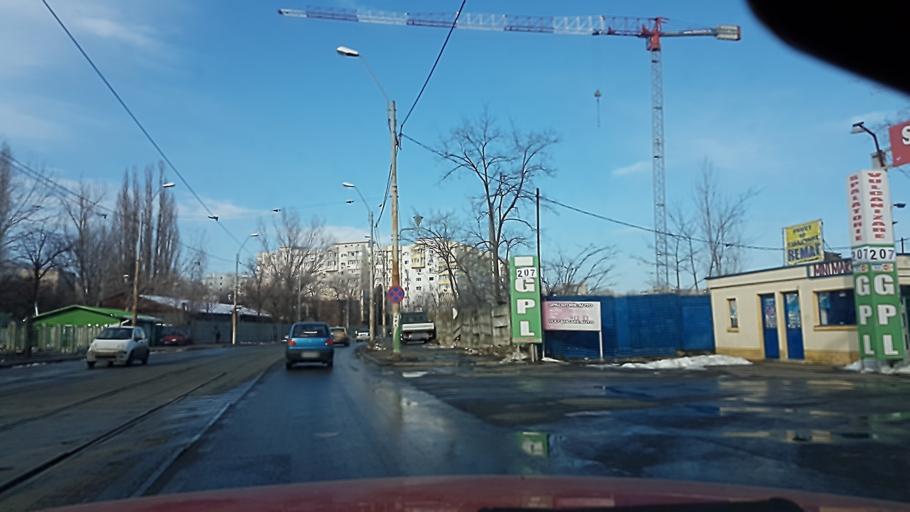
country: RO
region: Ilfov
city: Dobroesti
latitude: 44.4317
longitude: 26.1731
